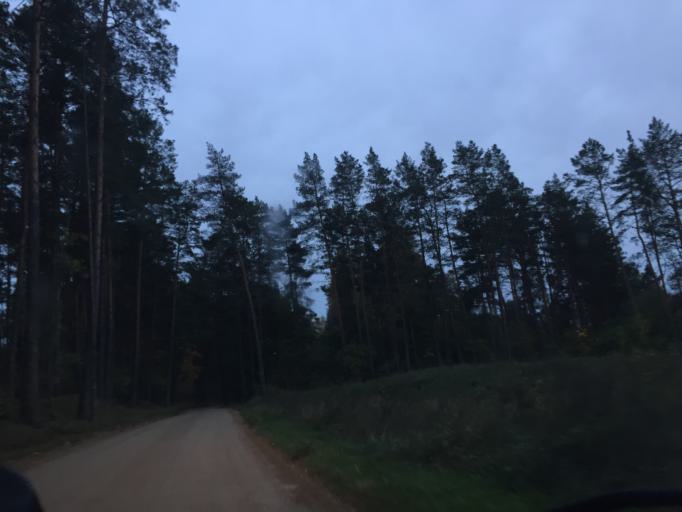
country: LV
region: Adazi
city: Adazi
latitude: 57.0862
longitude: 24.3486
